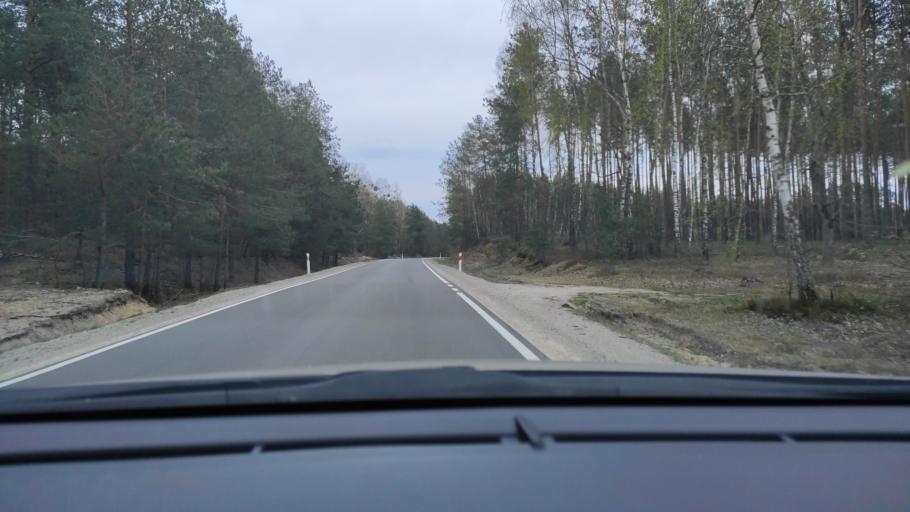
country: PL
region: Masovian Voivodeship
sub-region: Powiat zwolenski
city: Zwolen
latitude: 51.4071
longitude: 21.5252
